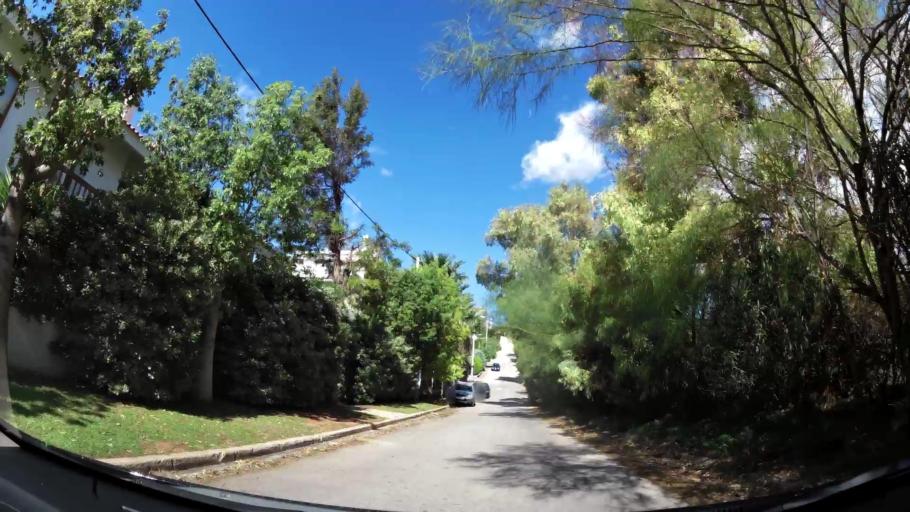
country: GR
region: Attica
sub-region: Nomarchia Anatolikis Attikis
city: Voula
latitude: 37.8437
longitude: 23.7846
